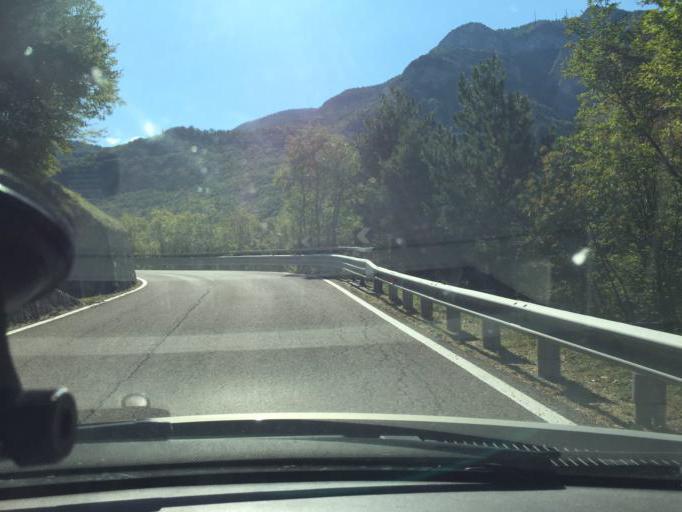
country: IT
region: Trentino-Alto Adige
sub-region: Provincia di Trento
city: Besenello
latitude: 45.9204
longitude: 11.1302
